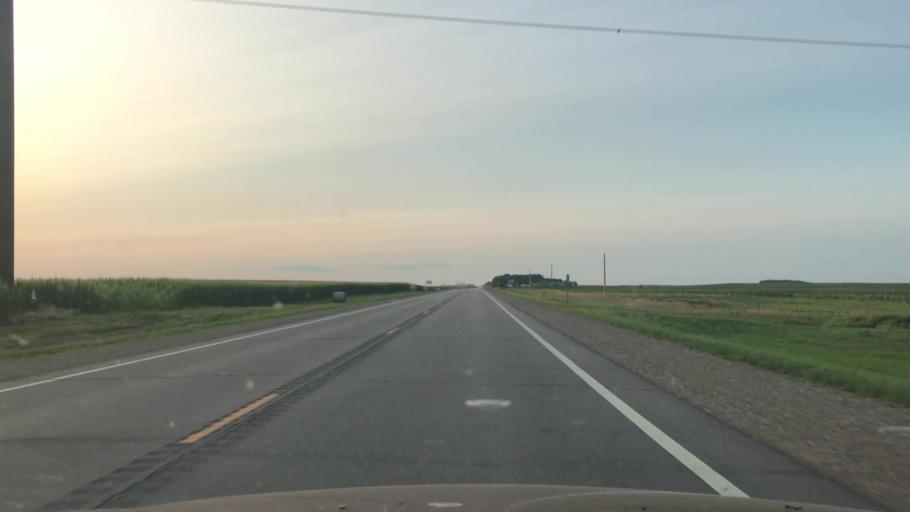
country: US
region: Minnesota
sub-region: Redwood County
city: Redwood Falls
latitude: 44.4340
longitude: -95.1176
